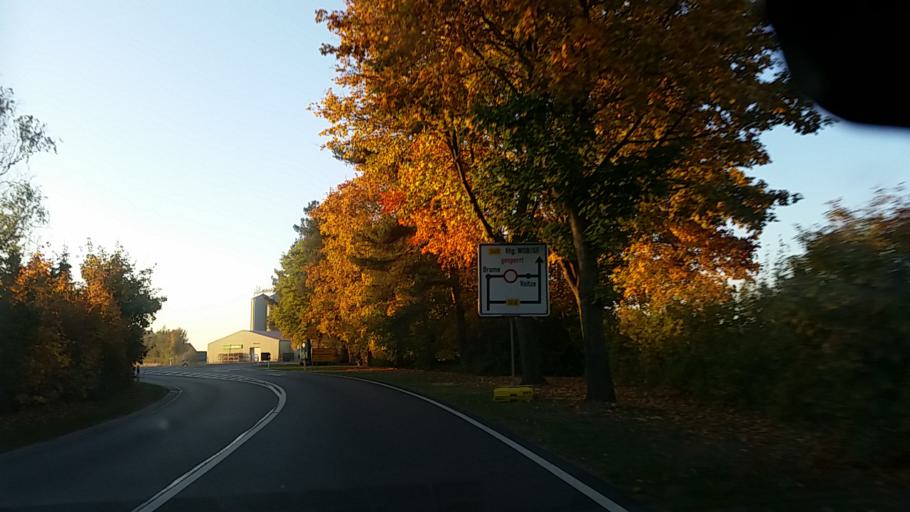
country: DE
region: Lower Saxony
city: Wittingen
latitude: 52.6944
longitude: 10.8082
